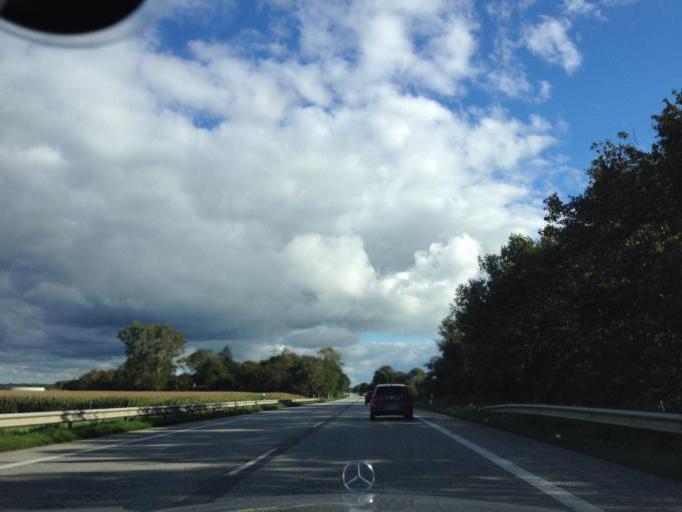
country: DE
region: Schleswig-Holstein
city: Risum-Lindholm
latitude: 54.7534
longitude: 8.8965
